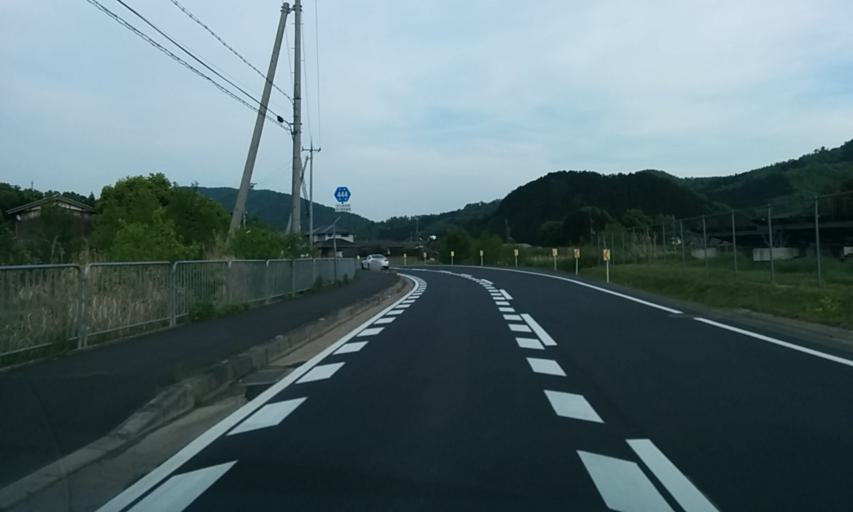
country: JP
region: Kyoto
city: Ayabe
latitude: 35.1625
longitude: 135.4059
